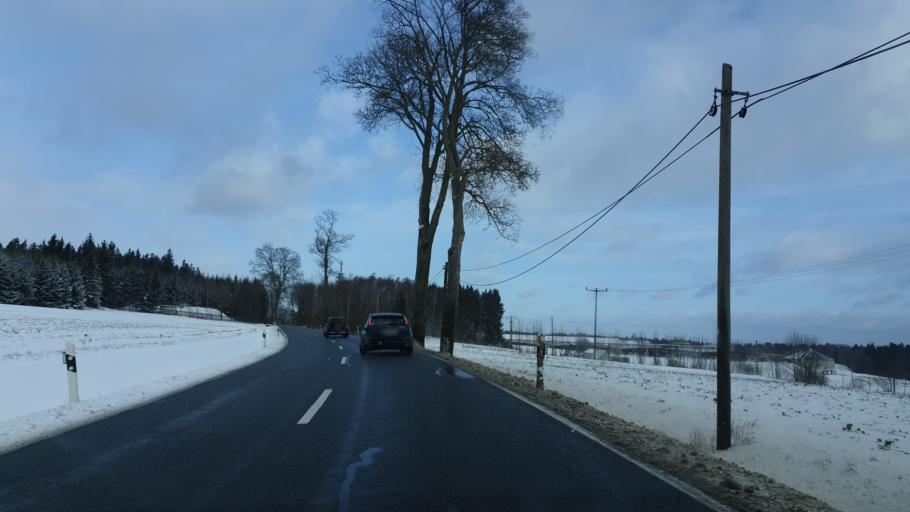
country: DE
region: Saxony
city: Eichigt
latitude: 50.3476
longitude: 12.1607
